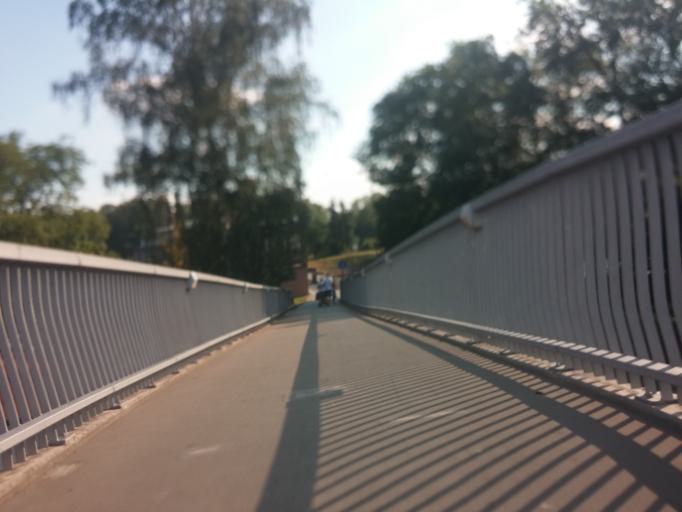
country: CZ
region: Central Bohemia
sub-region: Okres Nymburk
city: Podebrady
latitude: 50.1399
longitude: 15.1225
